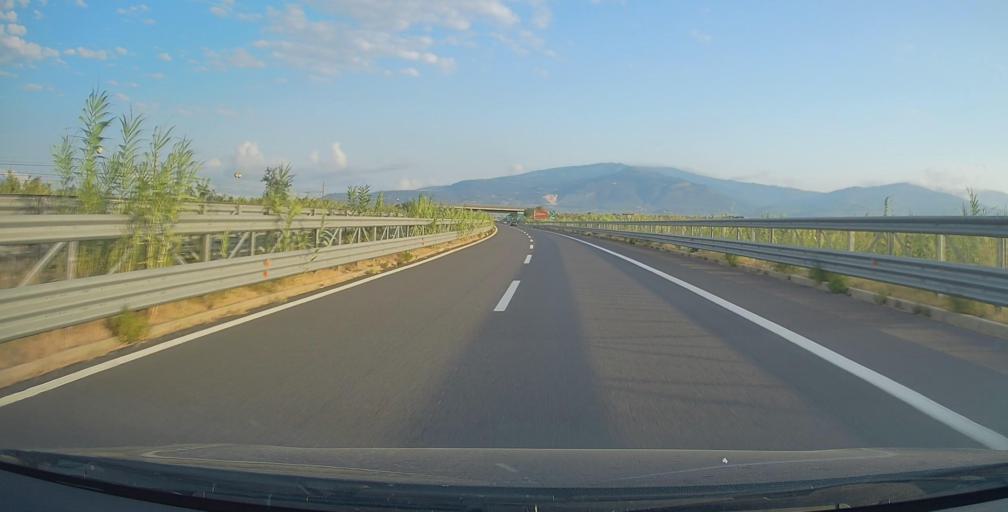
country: IT
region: Calabria
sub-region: Provincia di Catanzaro
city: Santa Eufemia Lamezia
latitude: 38.9049
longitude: 16.2767
